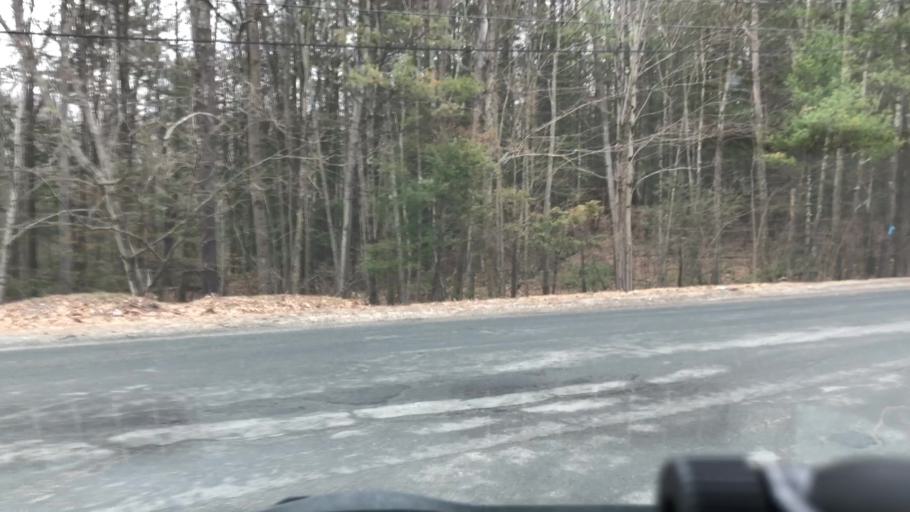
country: US
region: Massachusetts
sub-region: Hampshire County
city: Southampton
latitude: 42.2614
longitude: -72.7358
